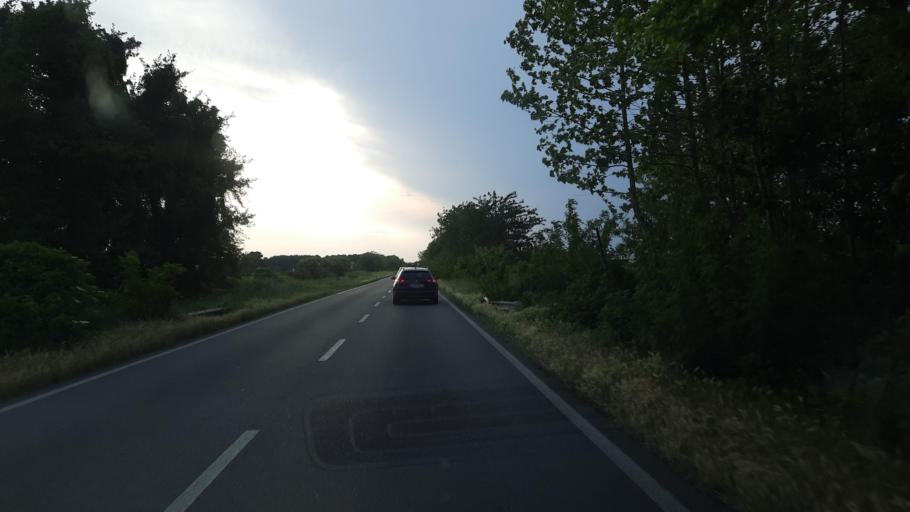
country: IT
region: Lombardy
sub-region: Provincia di Pavia
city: Garlasco
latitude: 45.1888
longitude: 8.9489
